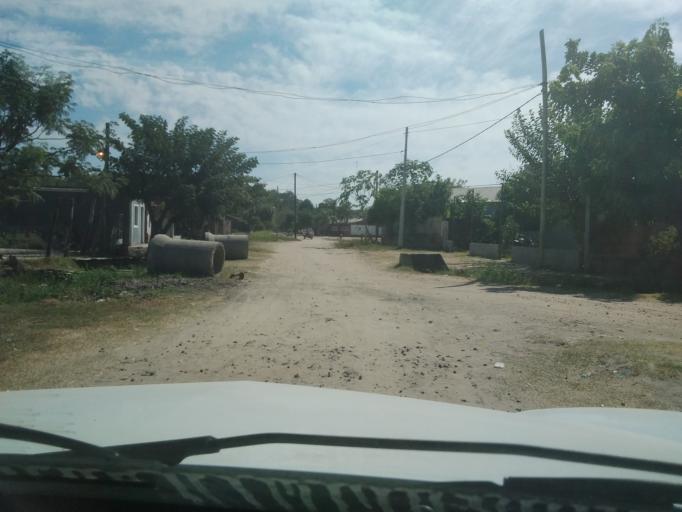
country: AR
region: Corrientes
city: Corrientes
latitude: -27.5112
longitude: -58.8019
